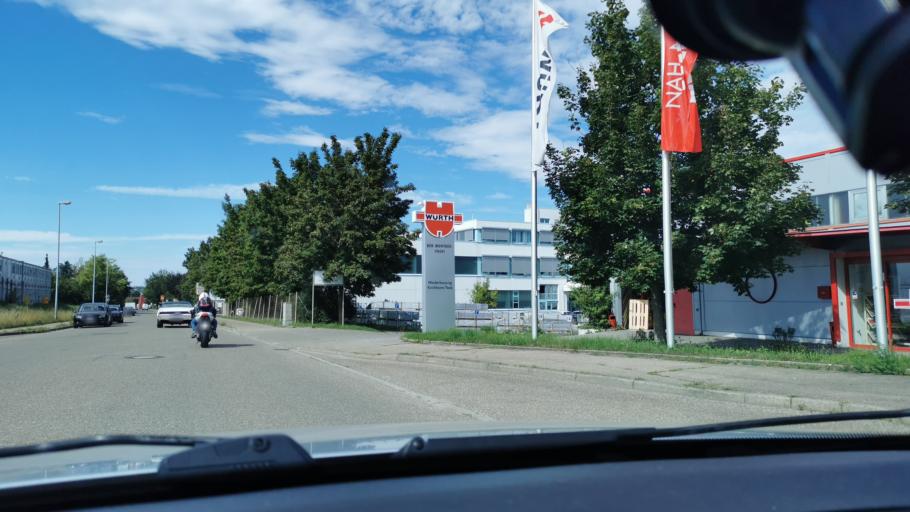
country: DE
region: Baden-Wuerttemberg
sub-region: Regierungsbezirk Stuttgart
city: Kirchheim unter Teck
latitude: 48.6344
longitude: 9.4676
